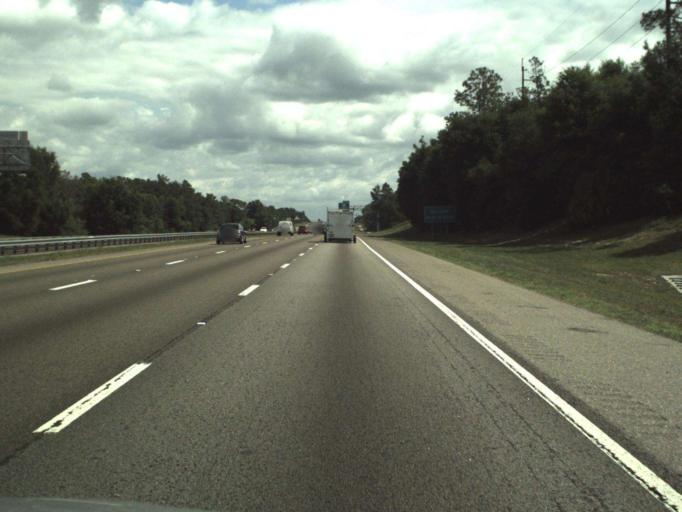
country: US
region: Florida
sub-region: Volusia County
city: Deltona
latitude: 28.9321
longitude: -81.2649
